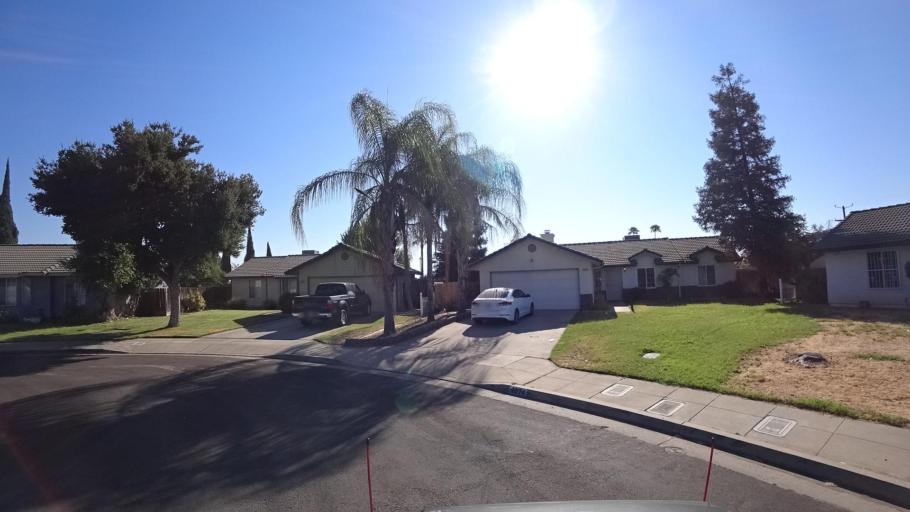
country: US
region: California
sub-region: Fresno County
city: Fresno
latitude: 36.7853
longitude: -119.7572
